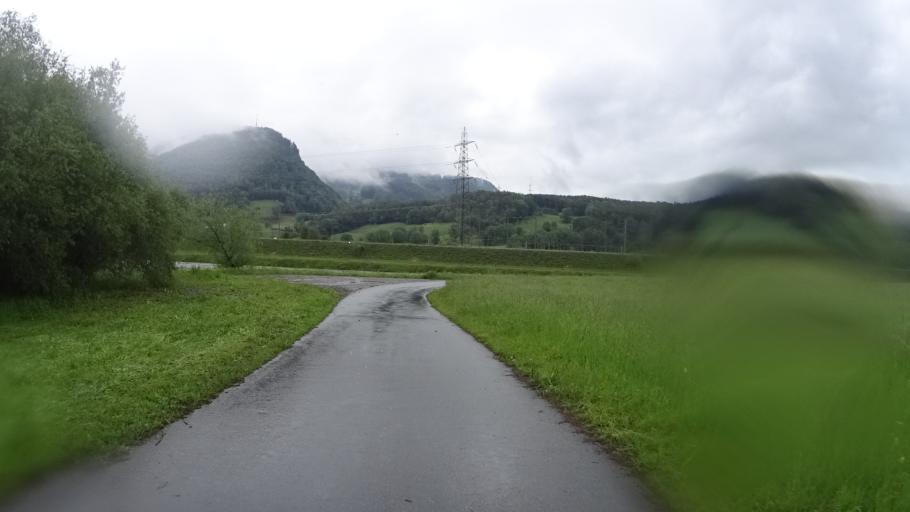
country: AT
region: Vorarlberg
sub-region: Politischer Bezirk Feldkirch
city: Meiningen
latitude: 47.2989
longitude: 9.5597
